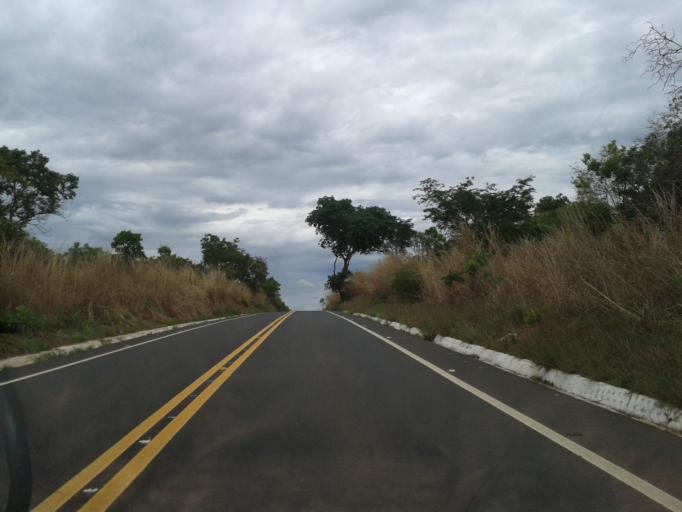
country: BR
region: Goias
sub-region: Caldas Novas
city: Caldas Novas
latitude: -17.8591
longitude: -48.6405
